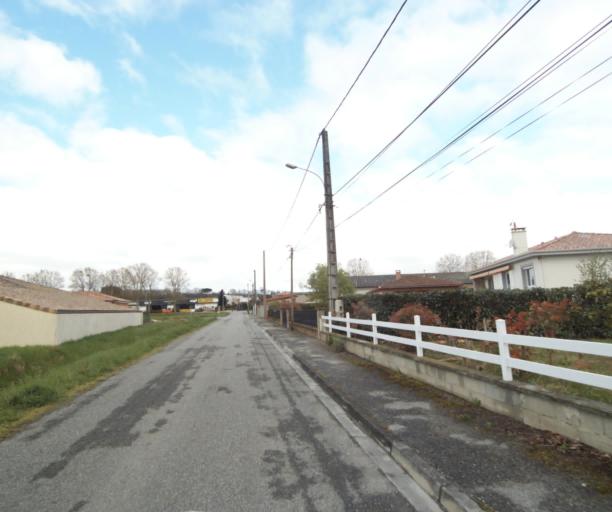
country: FR
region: Midi-Pyrenees
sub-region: Departement de l'Ariege
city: Saverdun
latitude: 43.2455
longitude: 1.5711
